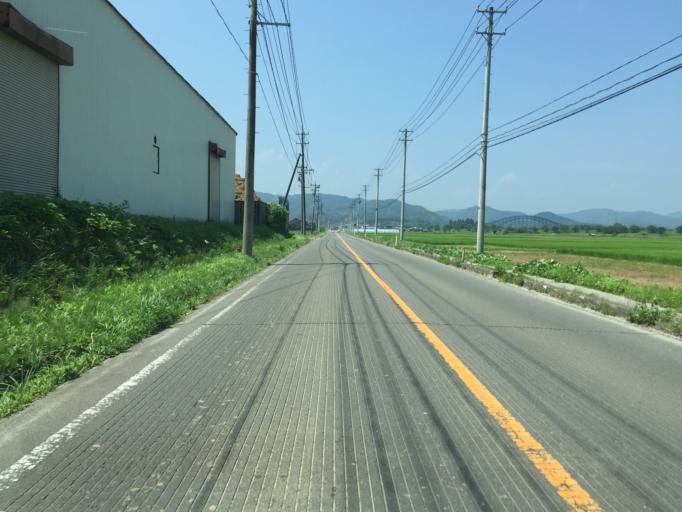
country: JP
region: Miyagi
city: Marumori
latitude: 37.9100
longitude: 140.7851
